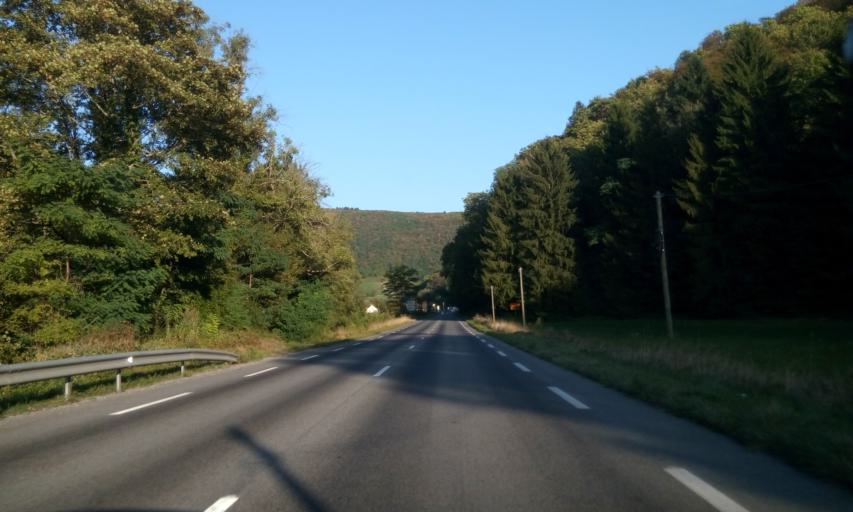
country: FR
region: Rhone-Alpes
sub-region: Departement de l'Ain
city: Poncin
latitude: 46.0757
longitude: 5.4374
